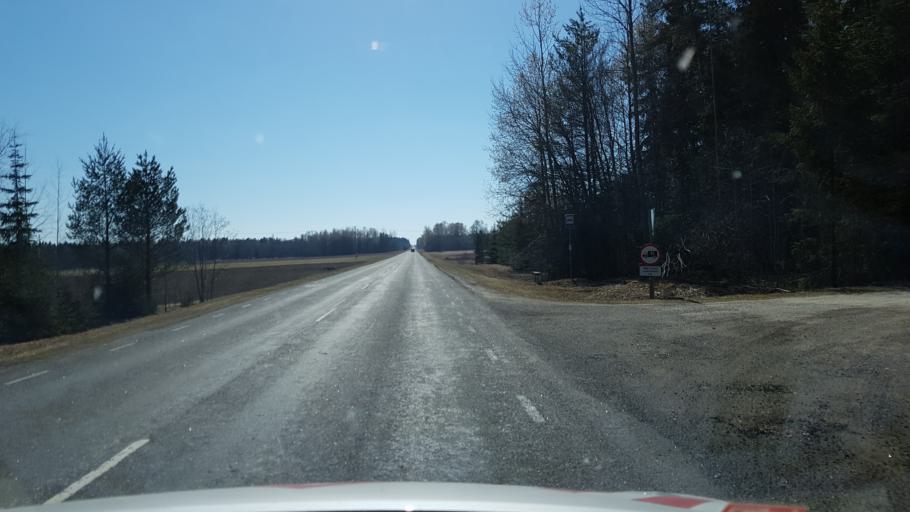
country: EE
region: Laeaene-Virumaa
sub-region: Tamsalu vald
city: Tamsalu
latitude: 59.1419
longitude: 26.0546
